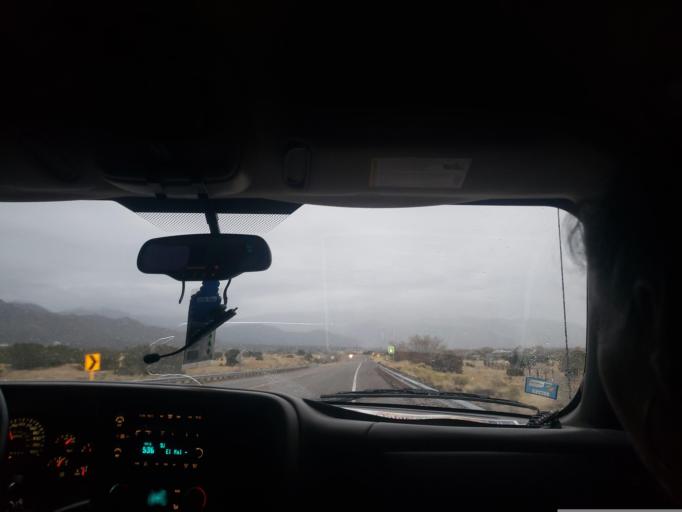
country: US
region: New Mexico
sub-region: Bernalillo County
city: Sandia Heights
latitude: 35.1996
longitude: -106.5054
